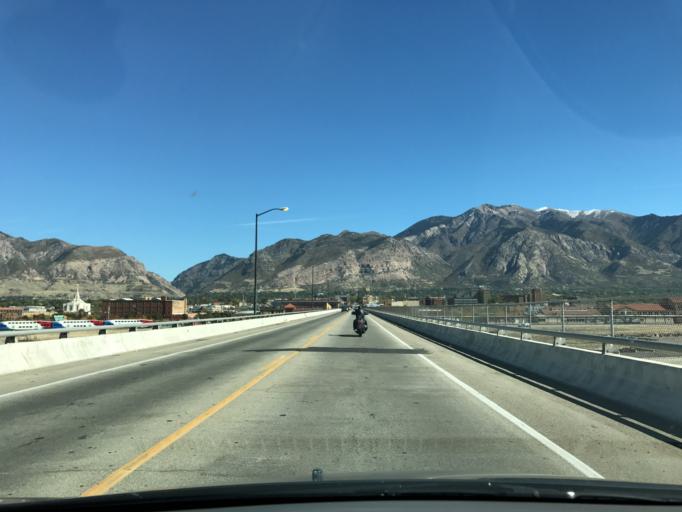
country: US
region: Utah
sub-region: Weber County
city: Ogden
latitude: 41.2229
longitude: -111.9842
